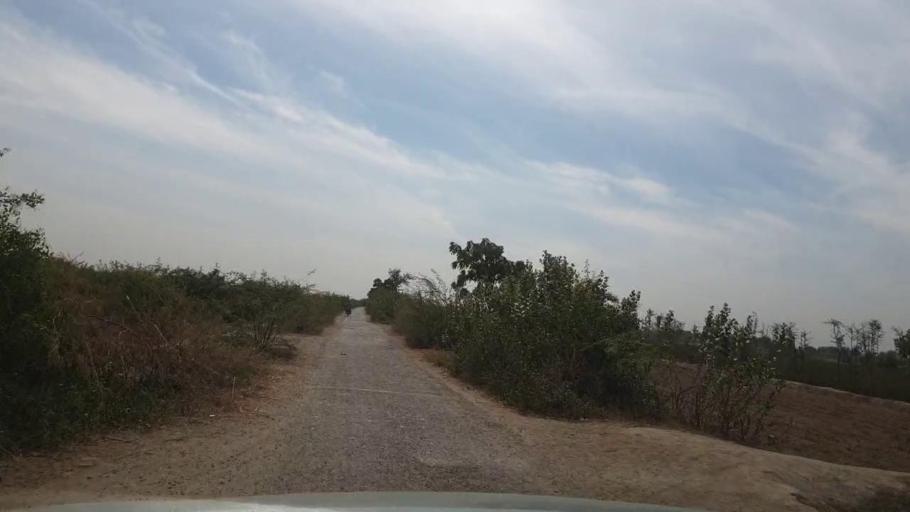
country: PK
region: Sindh
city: Nabisar
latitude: 25.0872
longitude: 69.5998
